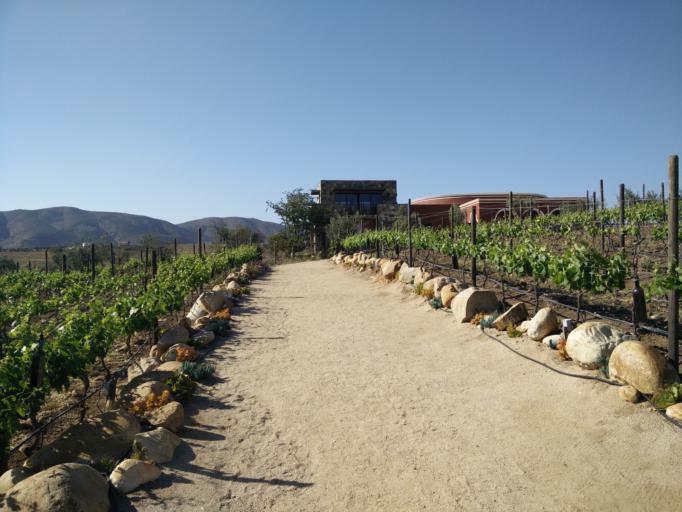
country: MX
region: Baja California
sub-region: Ensenada
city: Rancho Verde
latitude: 32.0165
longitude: -116.6636
